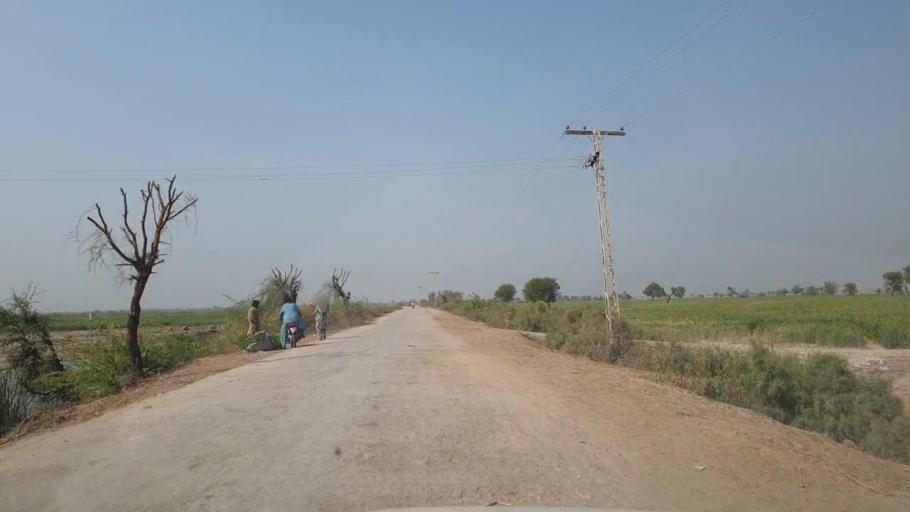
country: PK
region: Sindh
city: Mirpur Khas
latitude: 25.6920
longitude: 69.1498
